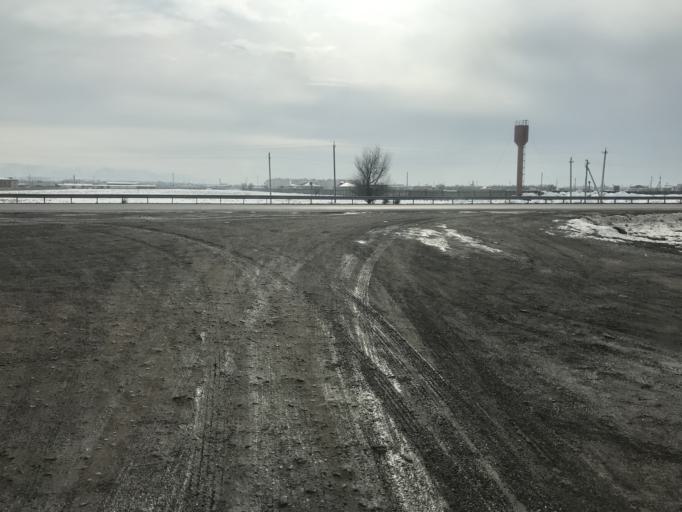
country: KZ
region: Ongtustik Qazaqstan
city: Aksu
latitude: 42.4747
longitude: 69.8187
